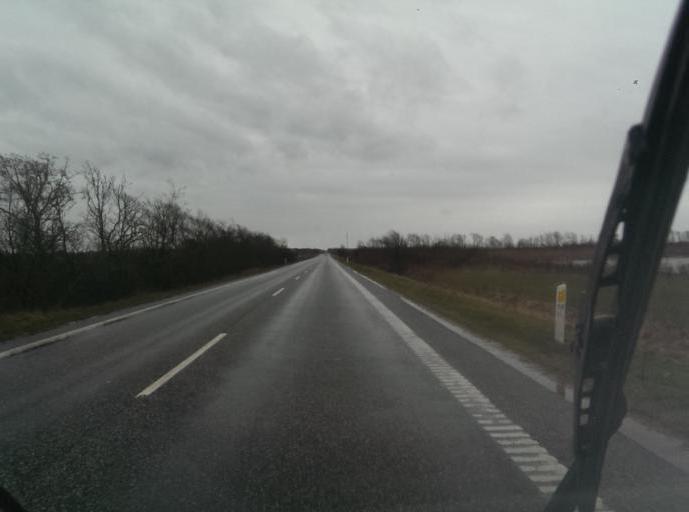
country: DK
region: Central Jutland
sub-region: Ringkobing-Skjern Kommune
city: Tarm
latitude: 55.8297
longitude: 8.4921
